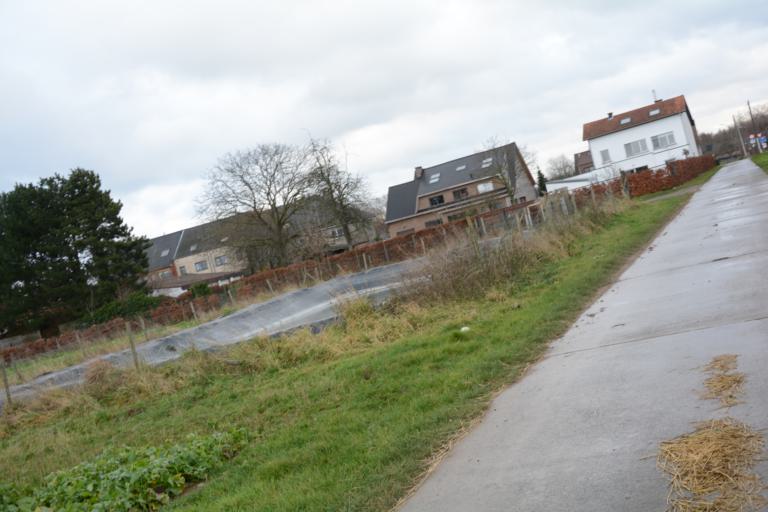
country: BE
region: Flanders
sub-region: Provincie Vlaams-Brabant
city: Merchtem
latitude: 50.9817
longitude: 4.2514
